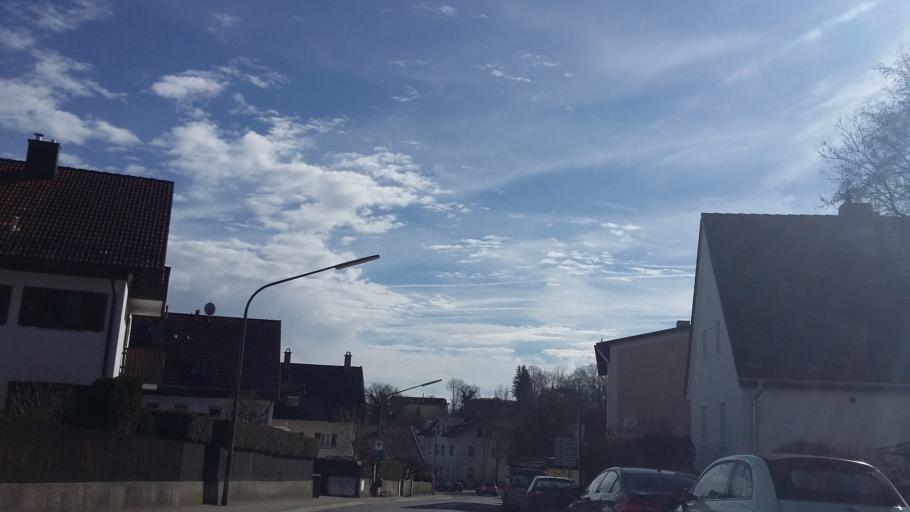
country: DE
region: Bavaria
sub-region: Upper Bavaria
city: Starnberg
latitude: 48.0033
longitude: 11.3403
